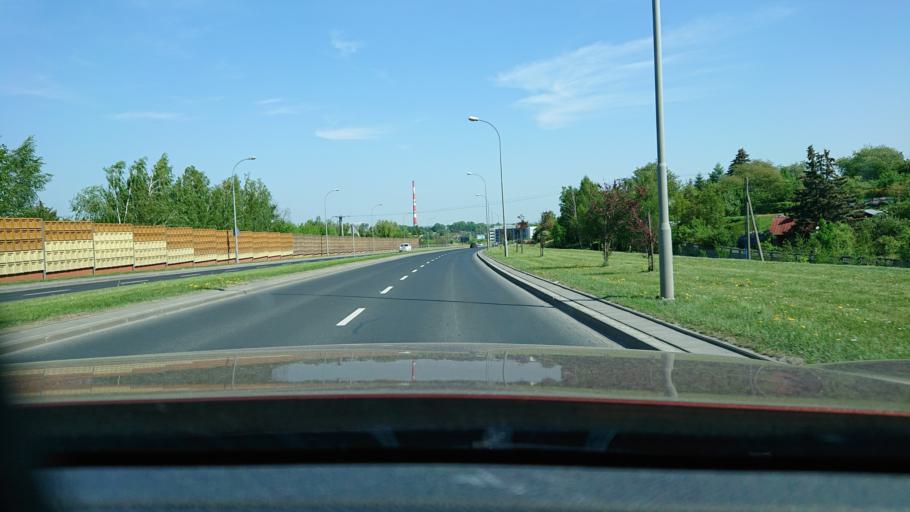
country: PL
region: Subcarpathian Voivodeship
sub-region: Rzeszow
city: Rzeszow
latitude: 50.0445
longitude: 22.0327
